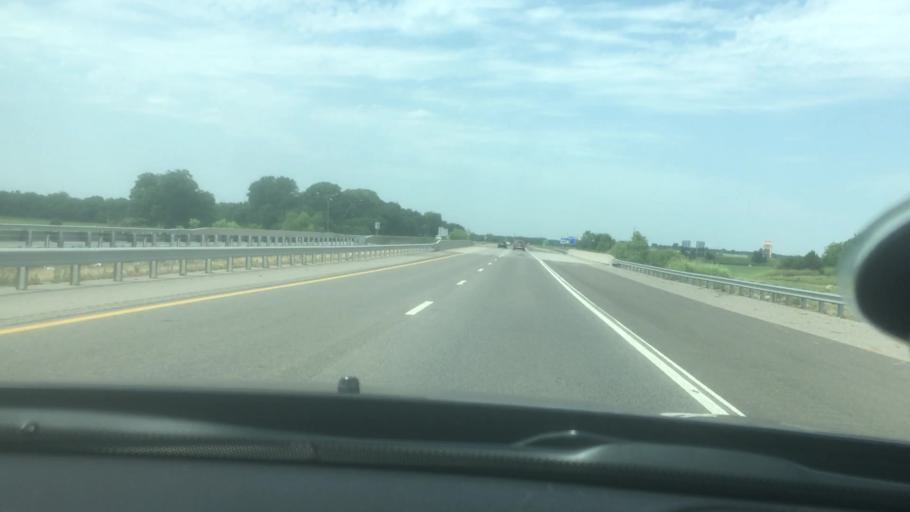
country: US
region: Oklahoma
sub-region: Pottawatomie County
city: Bethel Acres
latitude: 35.3782
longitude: -97.0344
